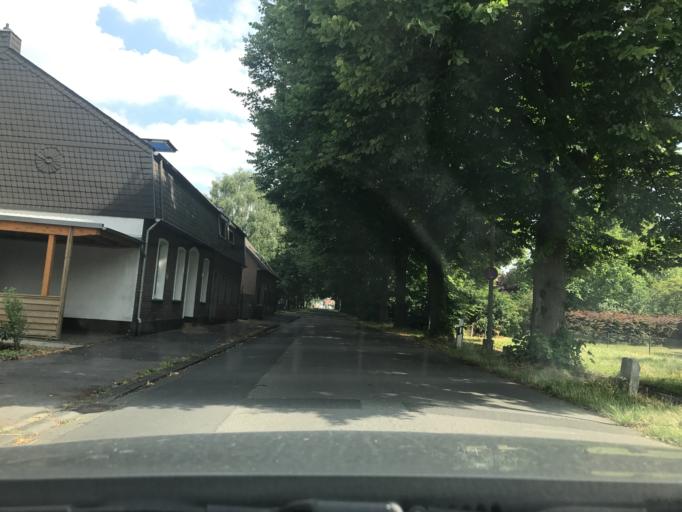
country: DE
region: North Rhine-Westphalia
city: Tonisvorst
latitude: 51.3763
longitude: 6.5000
